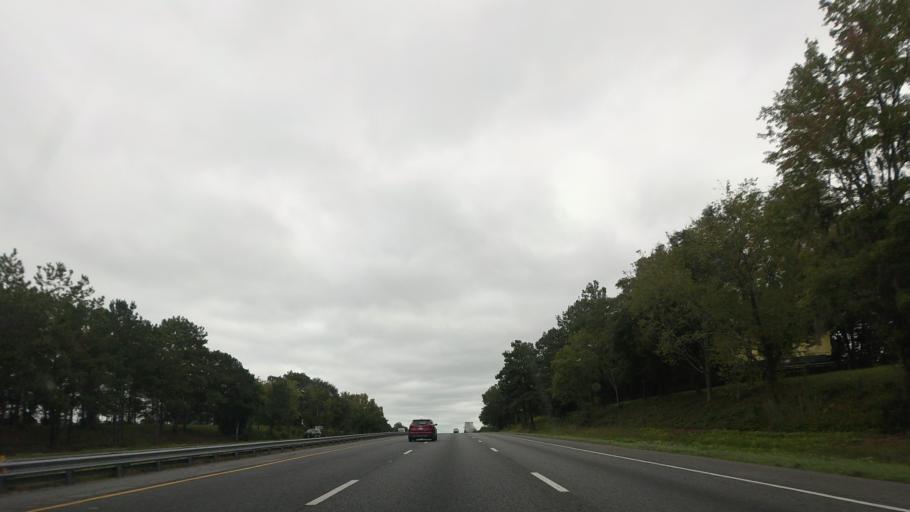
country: US
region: Florida
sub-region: Columbia County
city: Five Points
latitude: 30.2301
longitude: -82.7254
